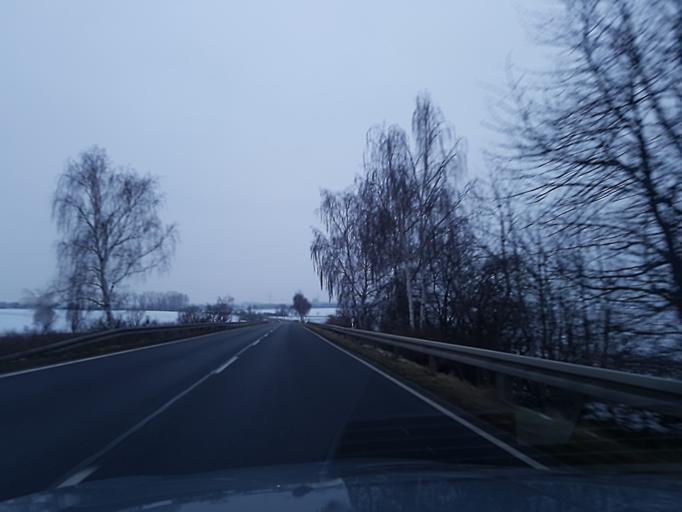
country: DE
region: Saxony
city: Ostrau
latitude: 51.2237
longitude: 13.1580
